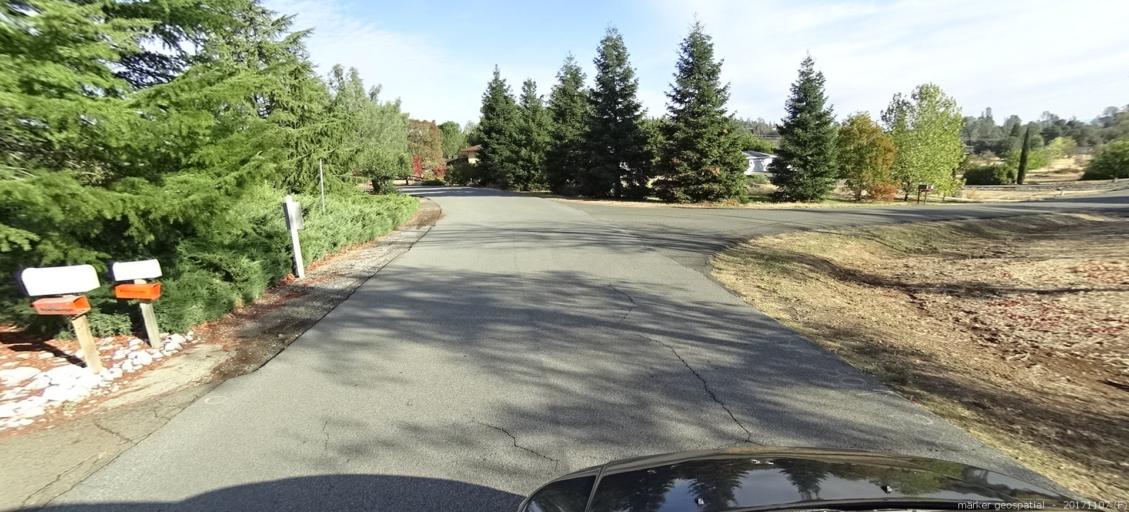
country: US
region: California
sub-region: Shasta County
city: Shasta
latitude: 40.5439
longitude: -122.4639
